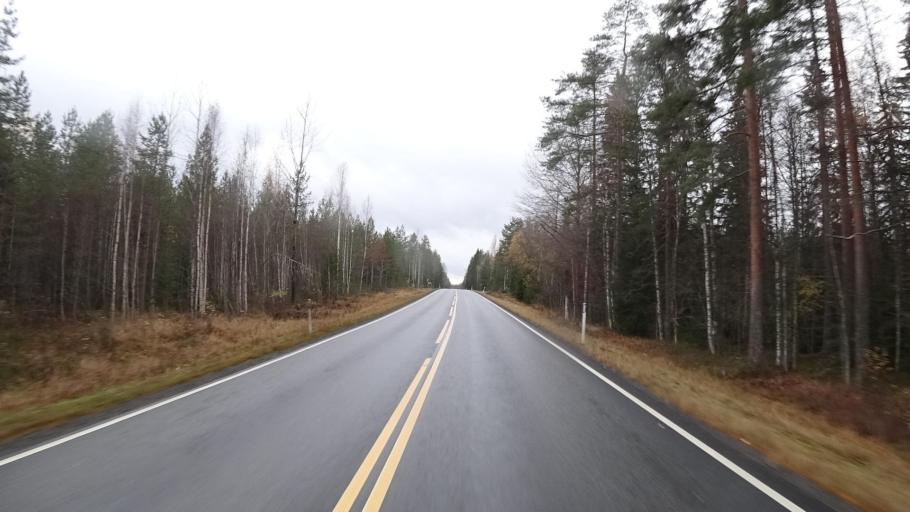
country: FI
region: Southern Savonia
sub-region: Mikkeli
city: Kangasniemi
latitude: 62.1591
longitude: 26.8279
